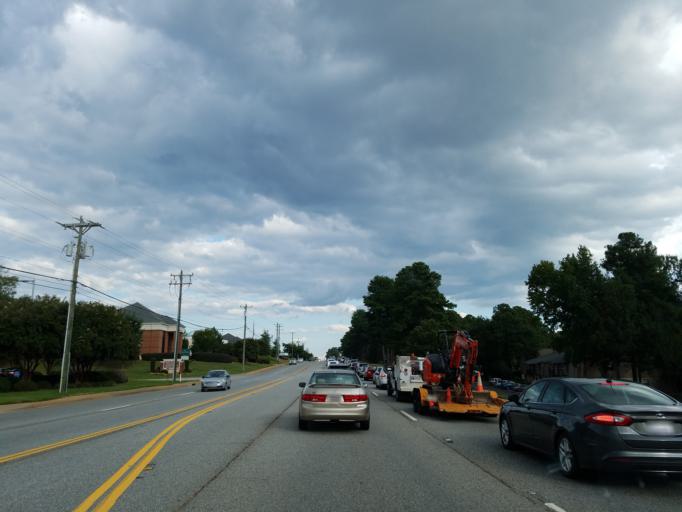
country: US
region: South Carolina
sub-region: Greenville County
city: Taylors
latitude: 34.8620
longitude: -82.2768
